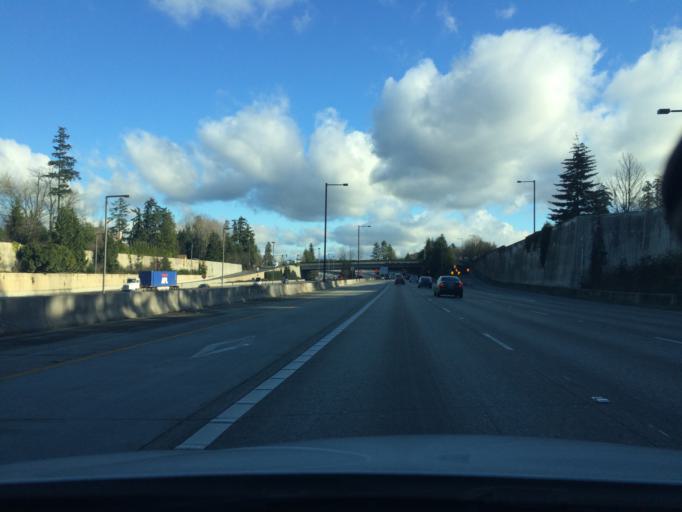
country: US
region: Washington
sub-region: King County
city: Mercer Island
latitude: 47.5786
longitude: -122.2124
